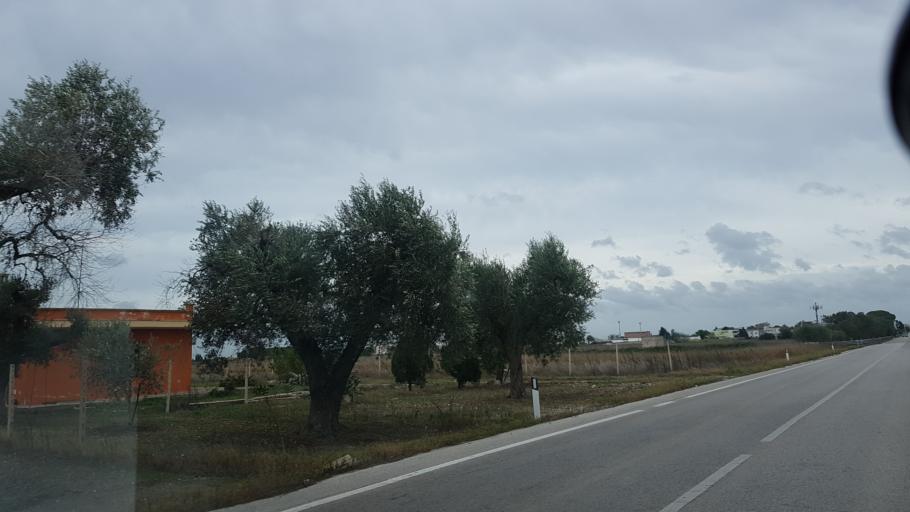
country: IT
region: Apulia
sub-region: Provincia di Lecce
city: Guagnano
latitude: 40.3994
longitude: 17.9332
